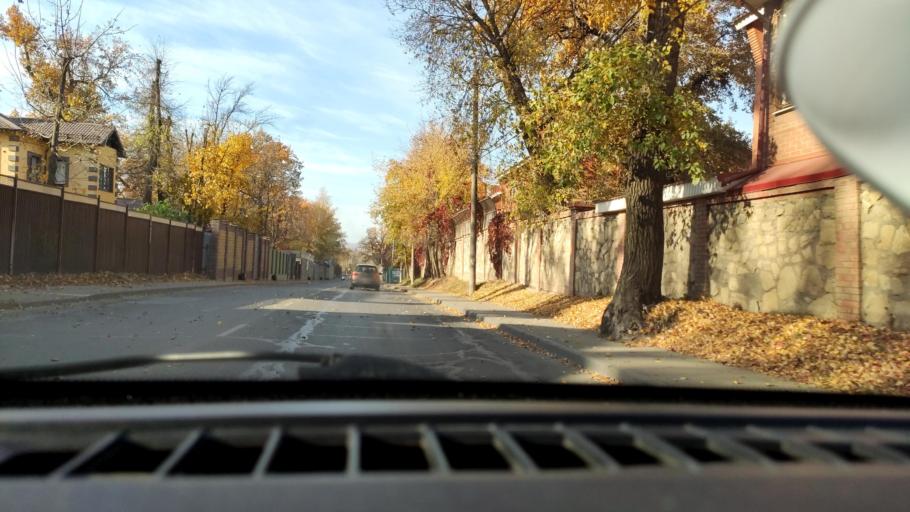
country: RU
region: Samara
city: Samara
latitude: 53.2719
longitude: 50.1941
